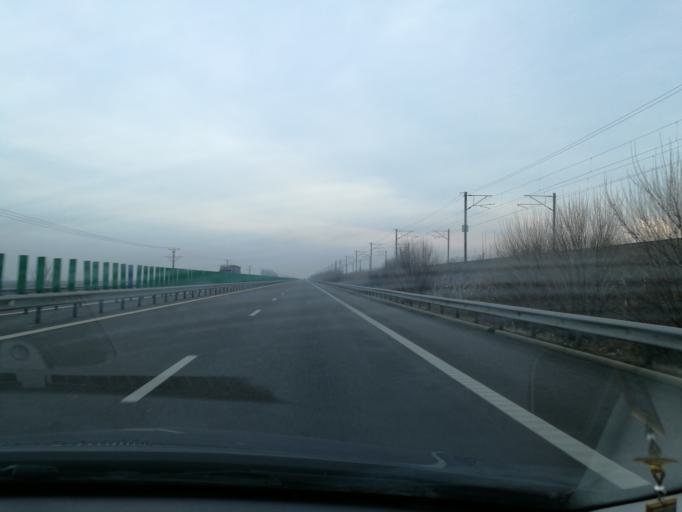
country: RO
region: Ialomita
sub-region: Comuna Stelnica
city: Stelnica
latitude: 44.3700
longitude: 27.8979
